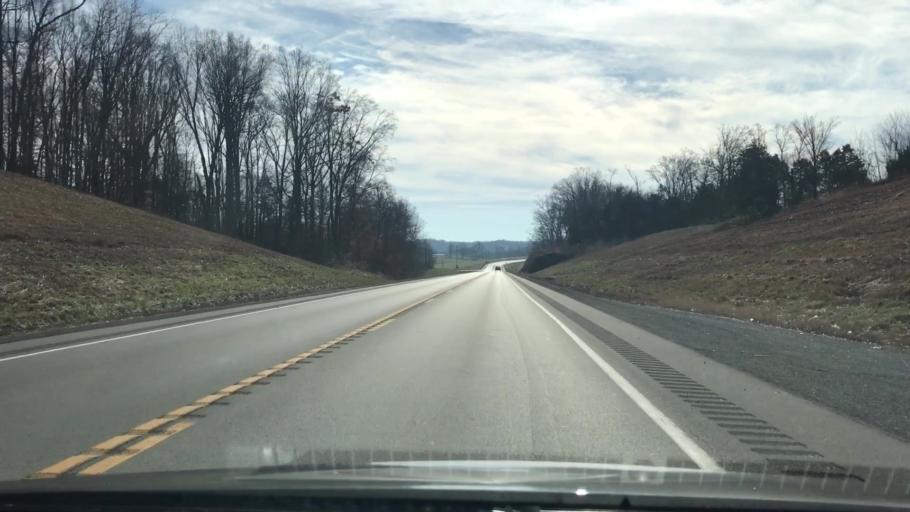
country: US
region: Kentucky
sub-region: Monroe County
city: Tompkinsville
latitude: 36.7661
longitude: -85.6858
